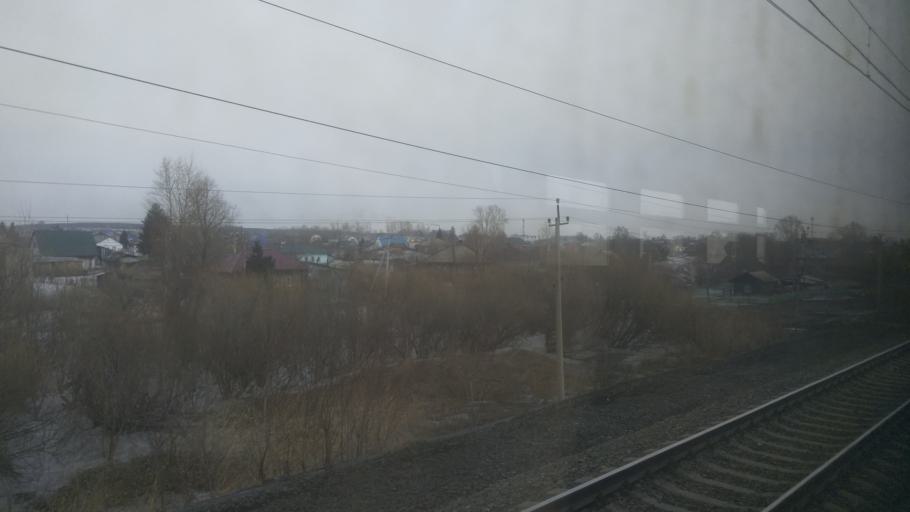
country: RU
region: Kemerovo
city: Yurga
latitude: 55.7104
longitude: 84.8295
